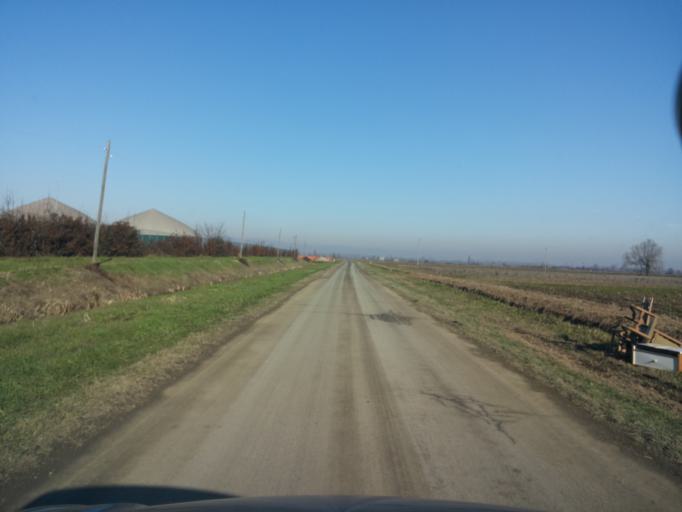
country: IT
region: Piedmont
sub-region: Provincia di Vercelli
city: San Germano Vercellese
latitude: 45.3728
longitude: 8.2419
